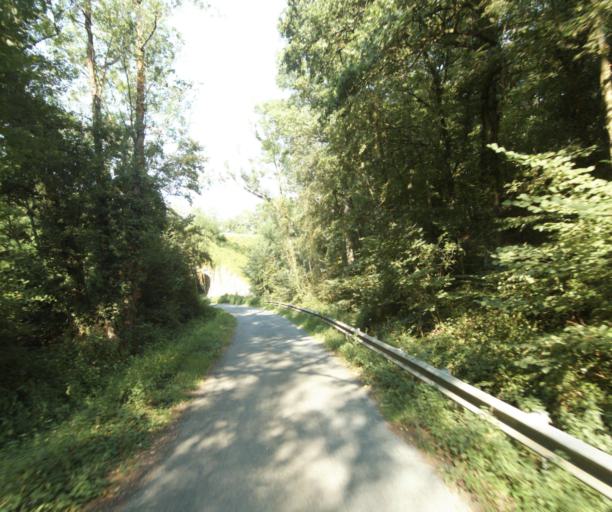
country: FR
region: Rhone-Alpes
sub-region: Departement du Rhone
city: Saint-Germain-Nuelles
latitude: 45.8359
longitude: 4.6002
